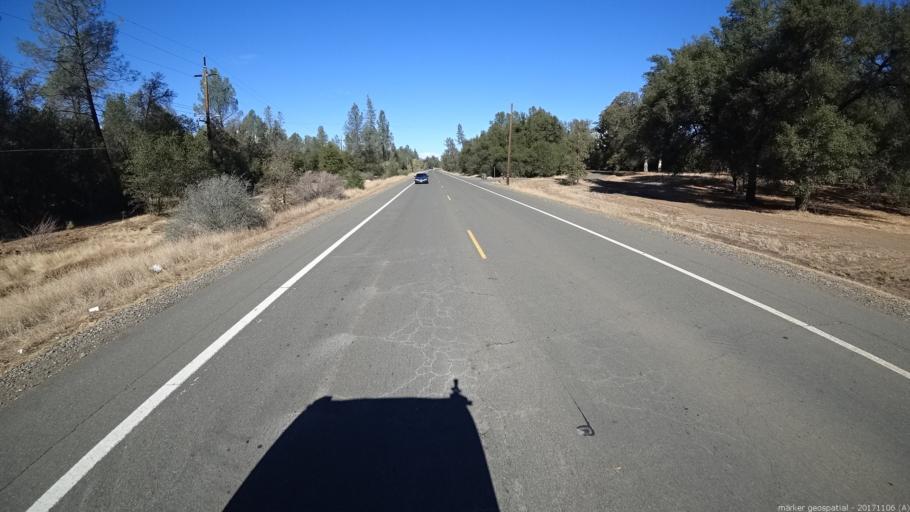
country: US
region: California
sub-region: Shasta County
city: Redding
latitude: 40.6045
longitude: -122.3148
